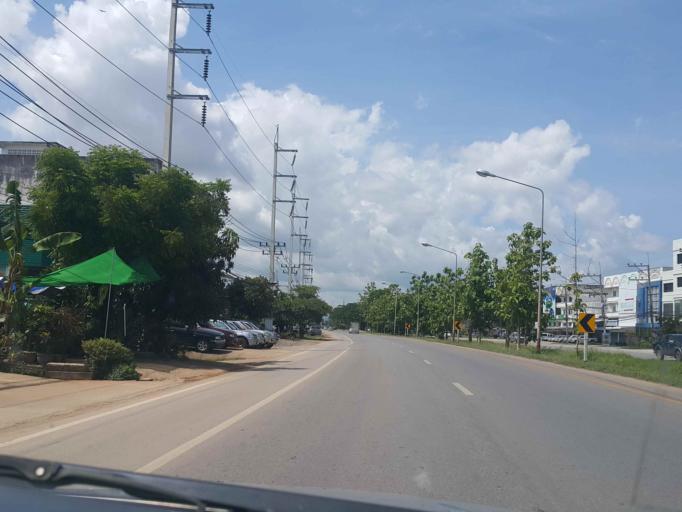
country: TH
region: Phayao
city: Phayao
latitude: 19.1545
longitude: 99.9133
